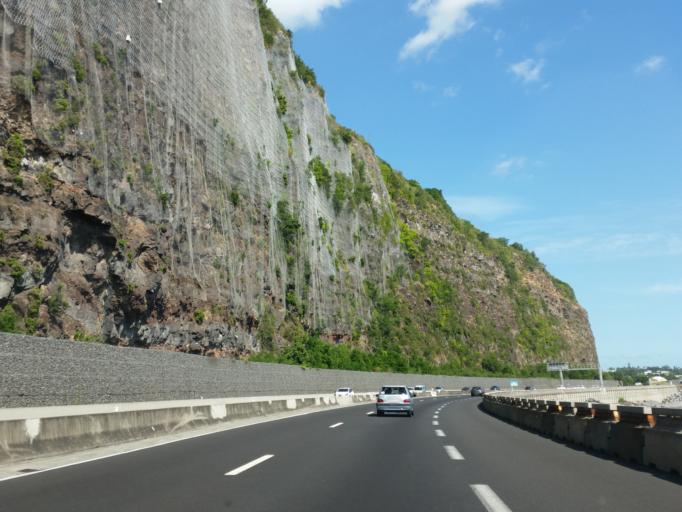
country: RE
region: Reunion
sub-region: Reunion
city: La Possession
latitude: -20.9174
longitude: 55.3493
